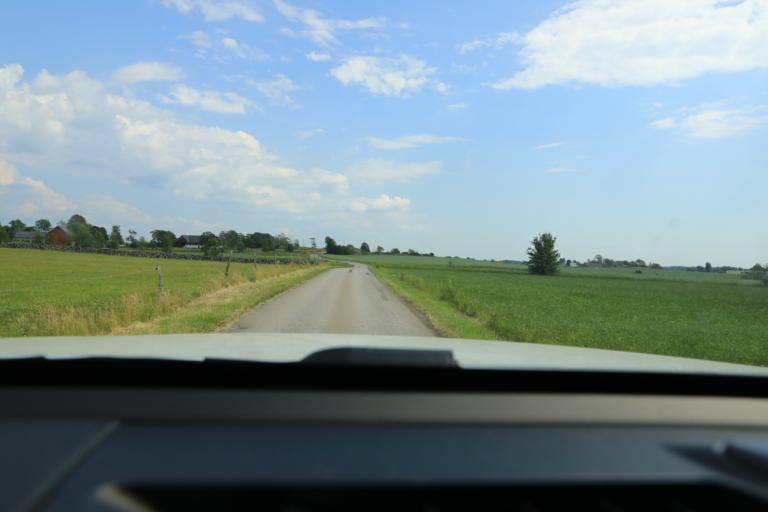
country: SE
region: Halland
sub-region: Varbergs Kommun
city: Varberg
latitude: 57.1397
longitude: 12.3241
